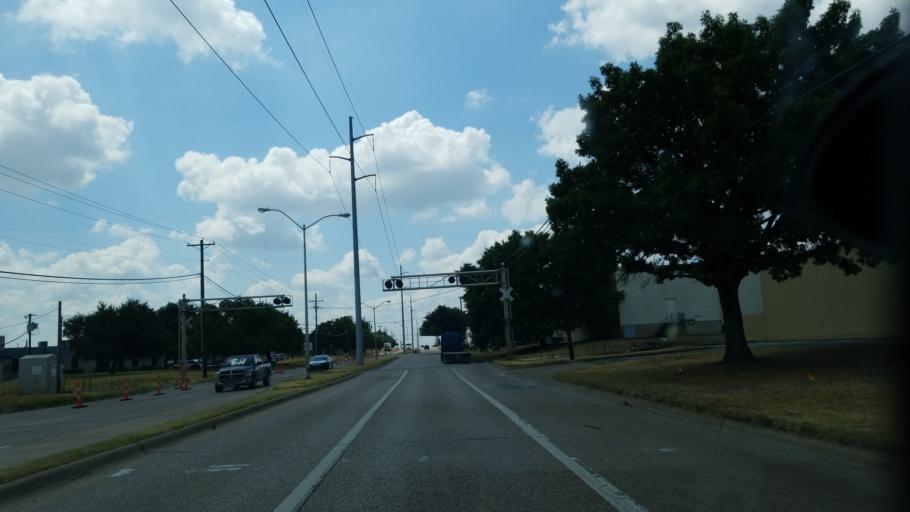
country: US
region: Texas
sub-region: Dallas County
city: Duncanville
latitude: 32.6869
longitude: -96.8915
